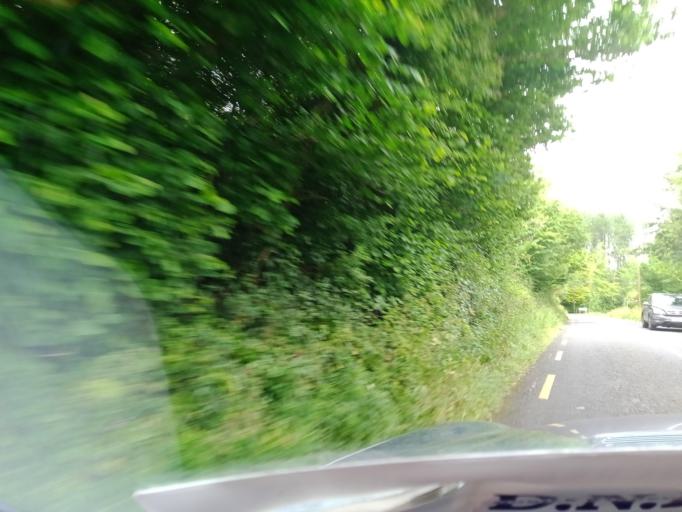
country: IE
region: Leinster
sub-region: Kilkenny
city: Piltown
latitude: 52.4700
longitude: -7.2757
